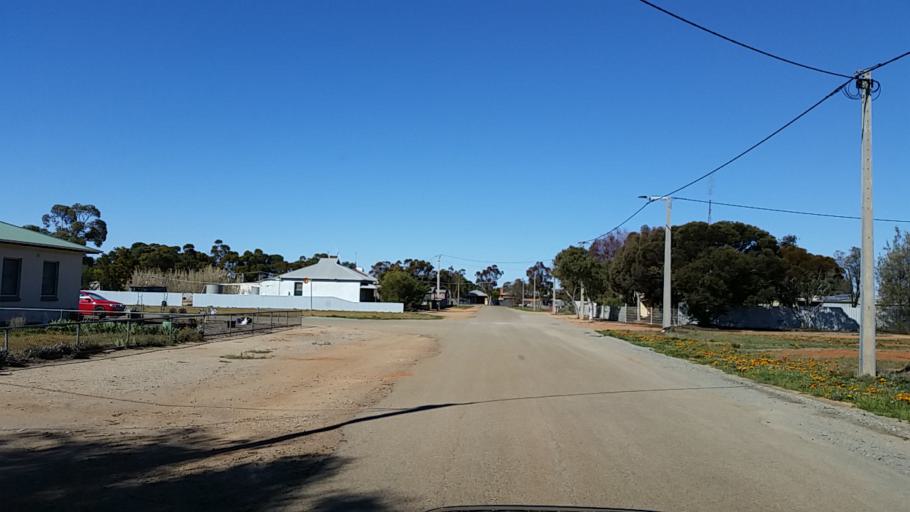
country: AU
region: South Australia
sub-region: Peterborough
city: Peterborough
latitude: -32.9787
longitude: 138.8405
